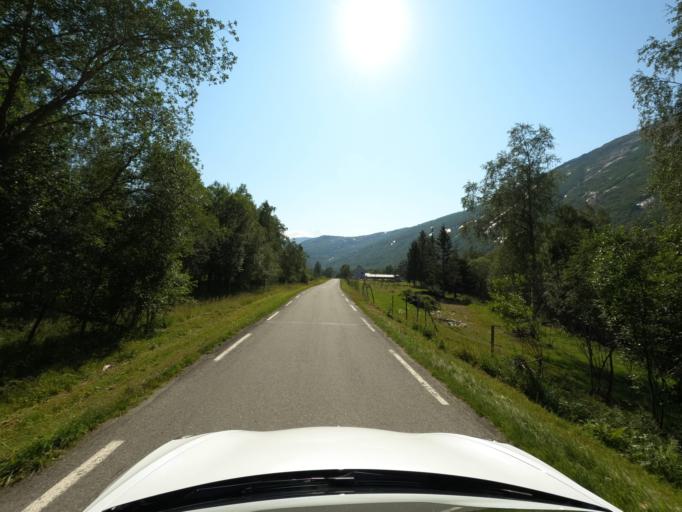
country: NO
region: Nordland
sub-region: Narvik
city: Narvik
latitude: 68.1838
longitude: 17.5561
